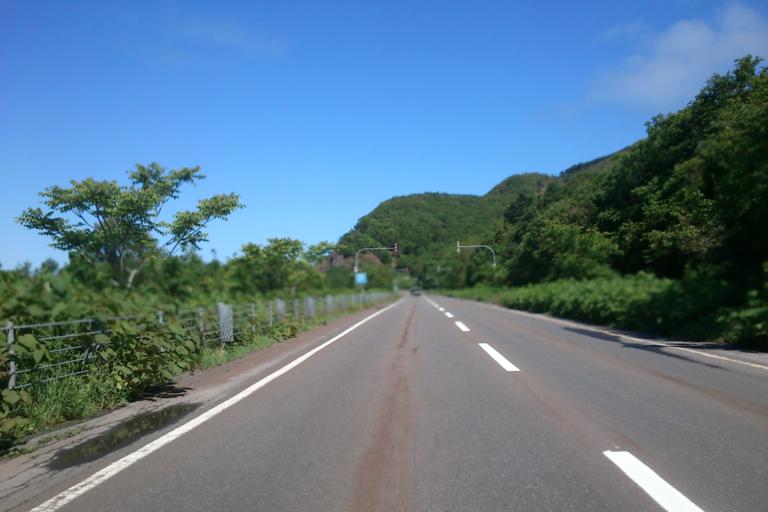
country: JP
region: Hokkaido
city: Ishikari
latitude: 43.4872
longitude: 141.3824
